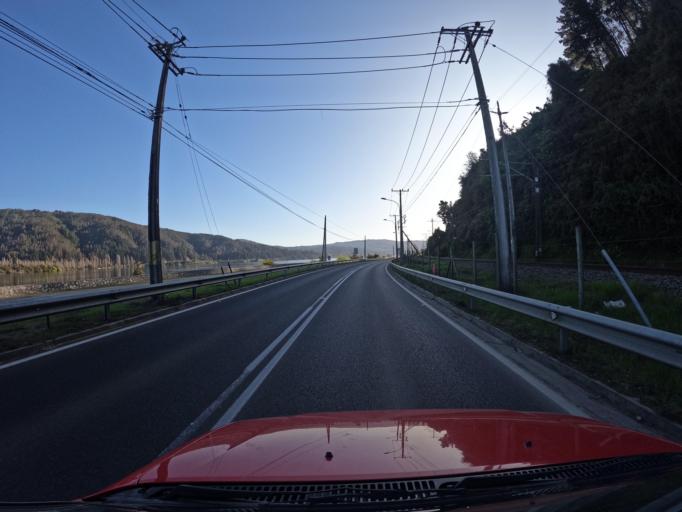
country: CL
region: Biobio
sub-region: Provincia de Concepcion
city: Chiguayante
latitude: -36.9702
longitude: -72.9743
